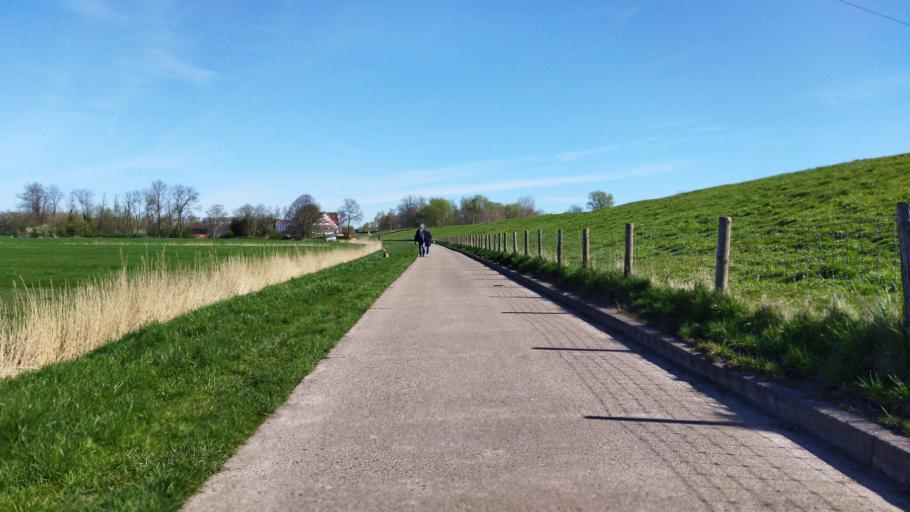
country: DE
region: Lower Saxony
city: Elsfleth
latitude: 53.2226
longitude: 8.4539
